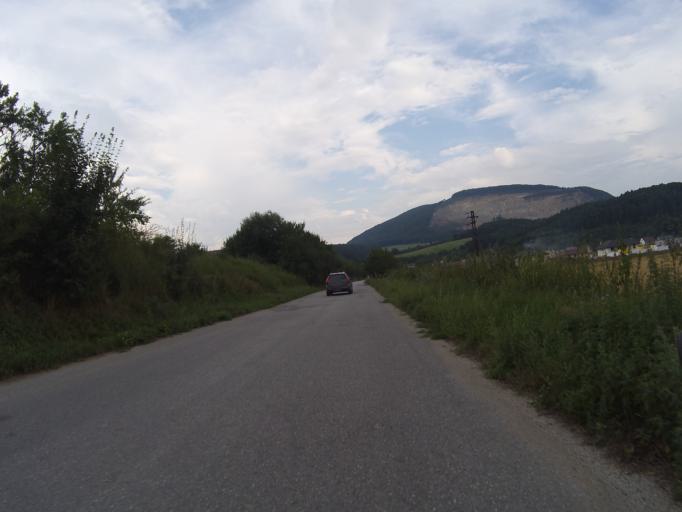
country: SK
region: Nitriansky
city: Ilava
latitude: 49.0403
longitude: 18.3072
